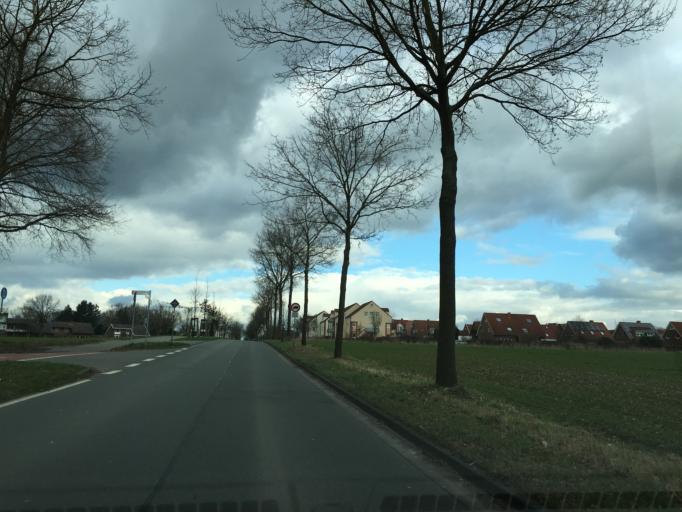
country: DE
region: North Rhine-Westphalia
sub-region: Regierungsbezirk Munster
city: Muenster
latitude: 51.9443
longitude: 7.6715
